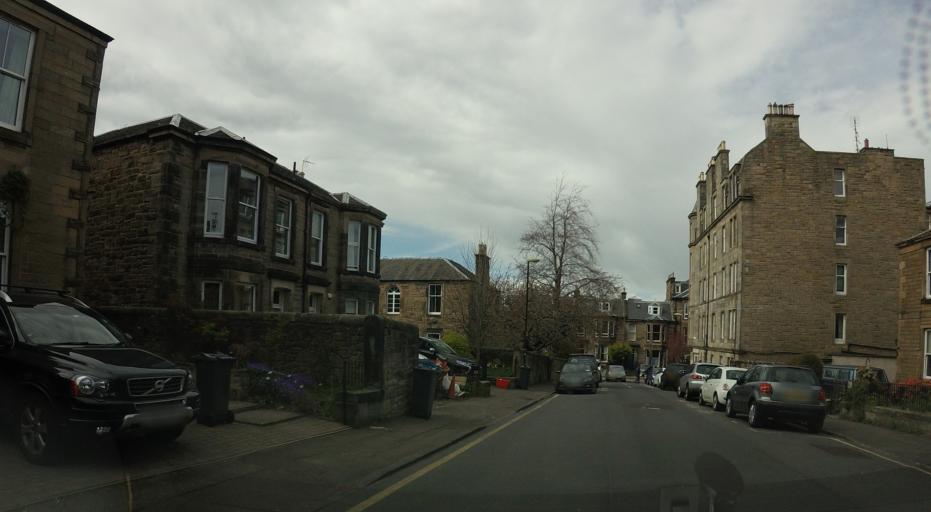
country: GB
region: Scotland
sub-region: Edinburgh
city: Edinburgh
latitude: 55.9385
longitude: -3.2132
